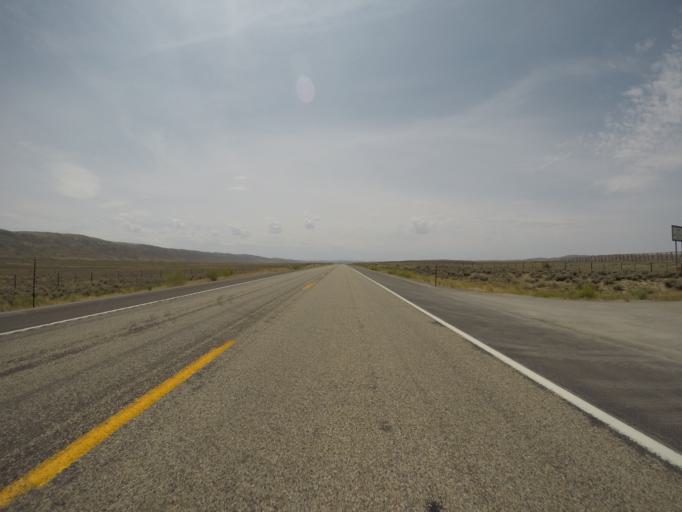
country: US
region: Wyoming
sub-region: Lincoln County
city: Kemmerer
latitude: 41.6793
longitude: -110.5683
